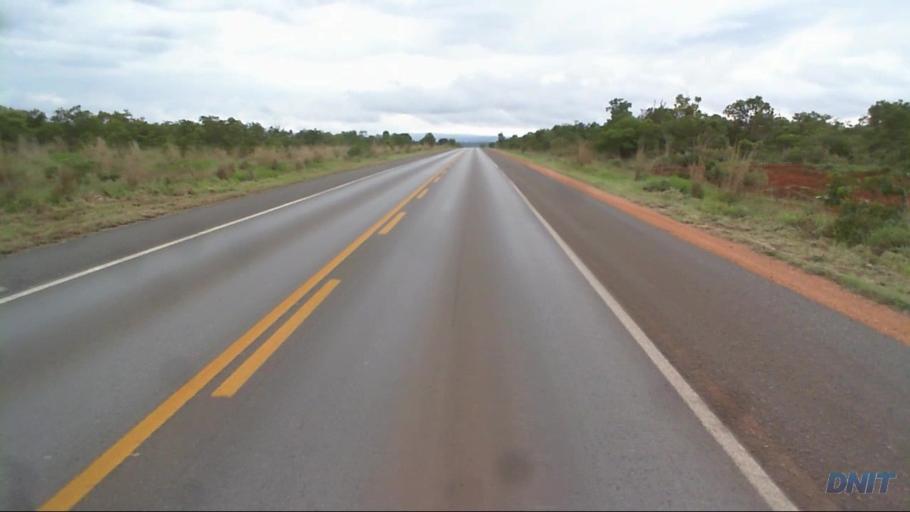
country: BR
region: Goias
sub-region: Barro Alto
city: Barro Alto
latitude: -15.2091
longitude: -48.6900
